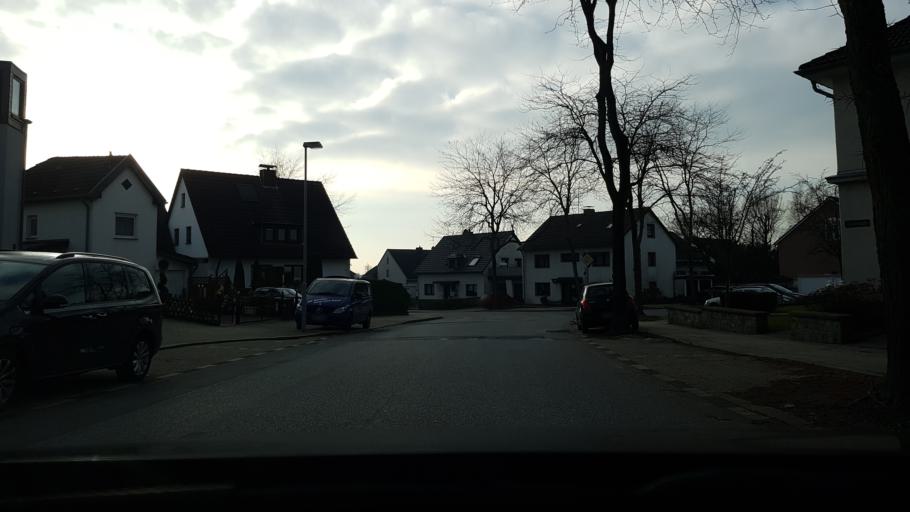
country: DE
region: North Rhine-Westphalia
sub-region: Regierungsbezirk Dusseldorf
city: Muelheim (Ruhr)
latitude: 51.4311
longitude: 6.9171
